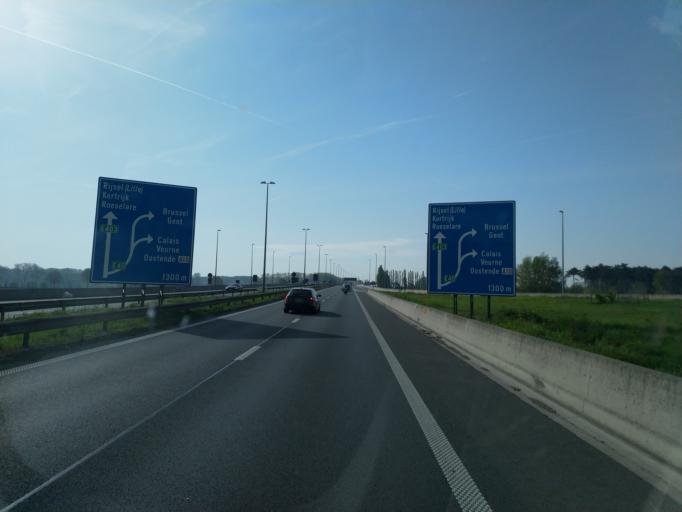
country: BE
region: Flanders
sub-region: Provincie West-Vlaanderen
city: Oostkamp
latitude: 51.1704
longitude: 3.2076
